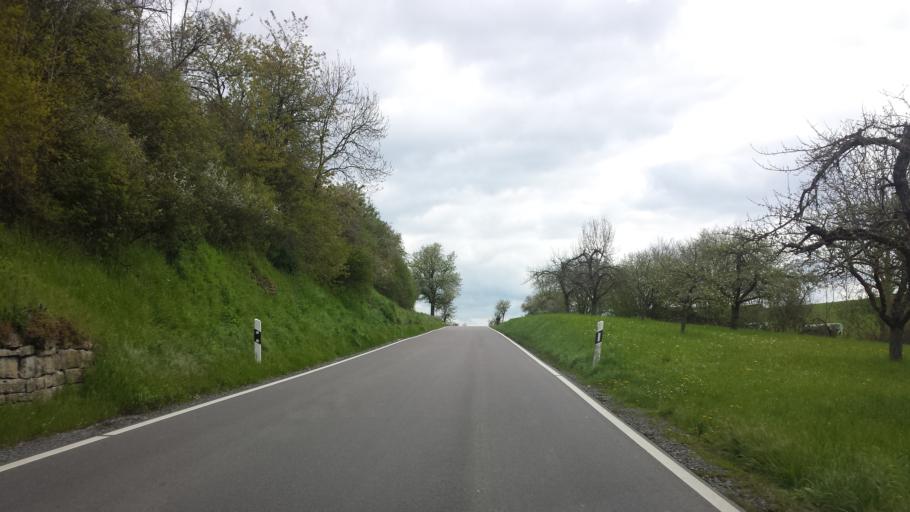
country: DE
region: Baden-Wuerttemberg
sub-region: Karlsruhe Region
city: Illingen
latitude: 48.9181
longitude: 8.9116
